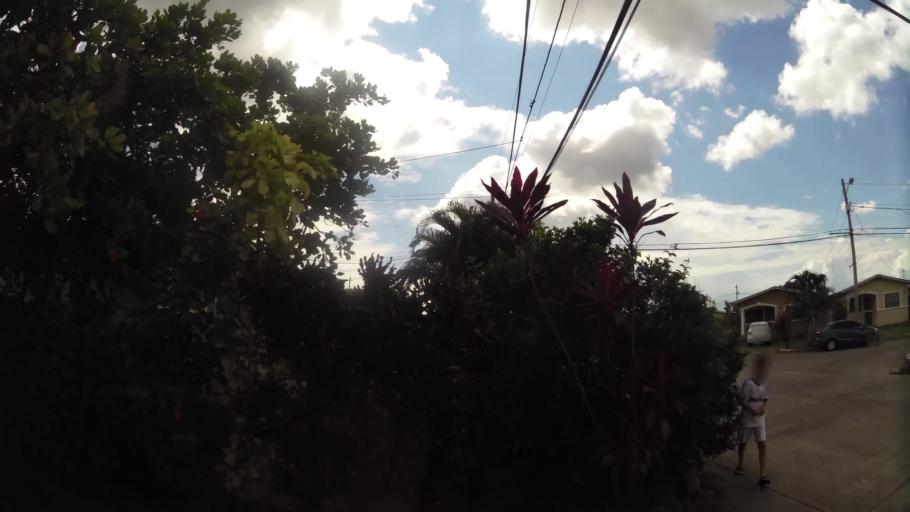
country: PA
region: Panama
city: Nuevo Arraijan
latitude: 8.9341
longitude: -79.7265
